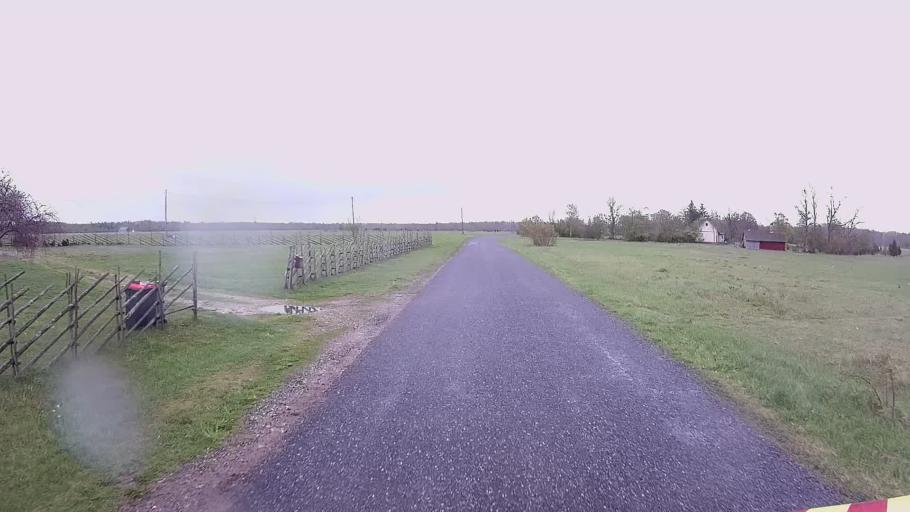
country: EE
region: Hiiumaa
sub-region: Kaerdla linn
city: Kardla
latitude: 58.6979
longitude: 22.5347
